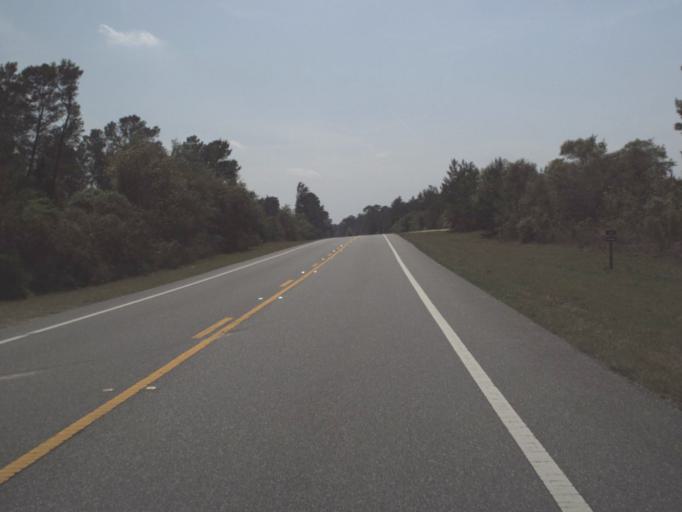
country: US
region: Florida
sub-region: Lake County
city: Astor
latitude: 29.1324
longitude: -81.6241
